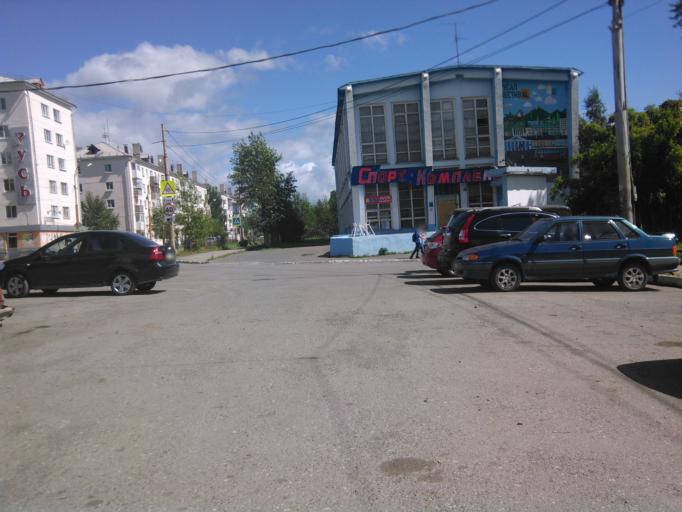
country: RU
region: Sverdlovsk
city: Krasnotur'insk
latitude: 59.7603
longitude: 60.1934
